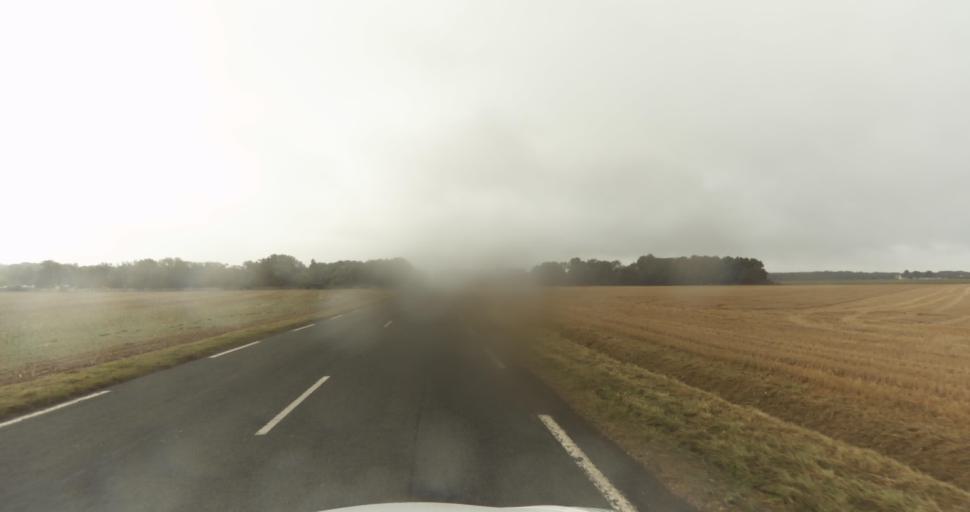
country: FR
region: Haute-Normandie
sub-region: Departement de l'Eure
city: Normanville
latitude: 49.1010
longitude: 1.1730
